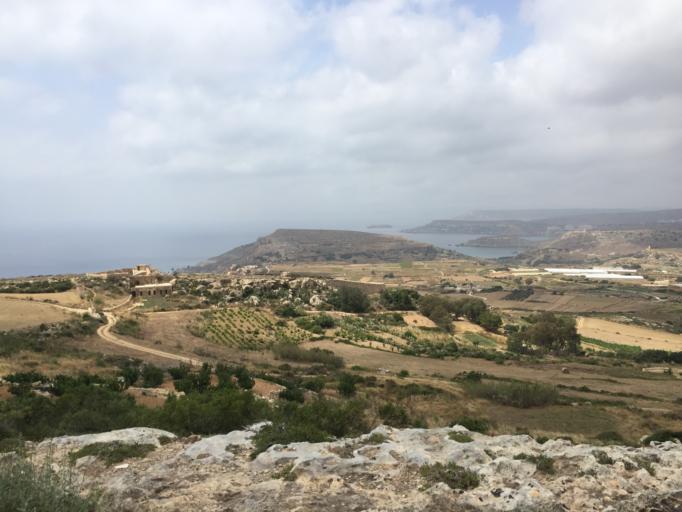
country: MT
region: L-Imgarr
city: Imgarr
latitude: 35.9016
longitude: 14.3490
